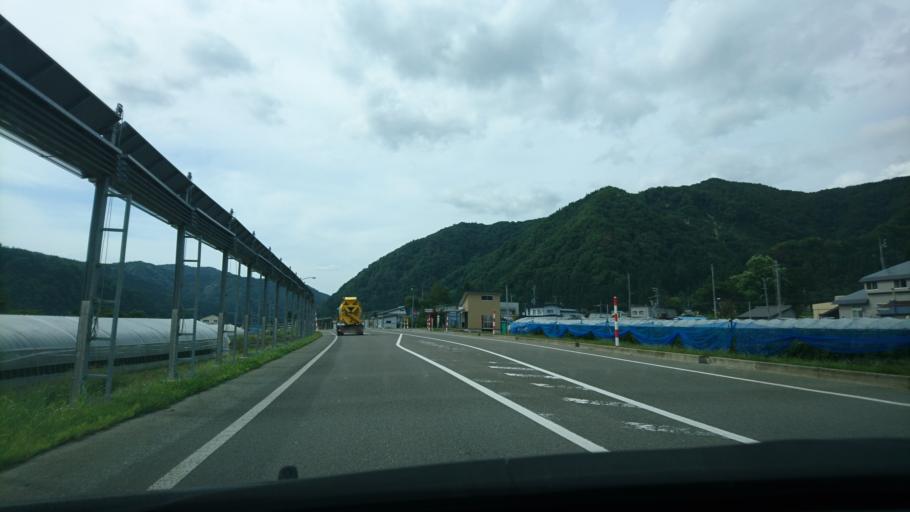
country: JP
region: Akita
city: Yuzawa
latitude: 39.1755
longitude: 140.6994
